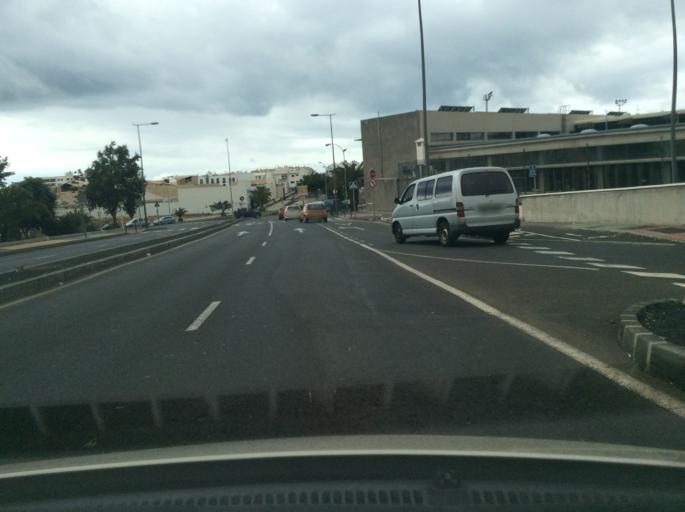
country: ES
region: Canary Islands
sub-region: Provincia de Las Palmas
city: Arrecife
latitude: 28.9697
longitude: -13.5470
